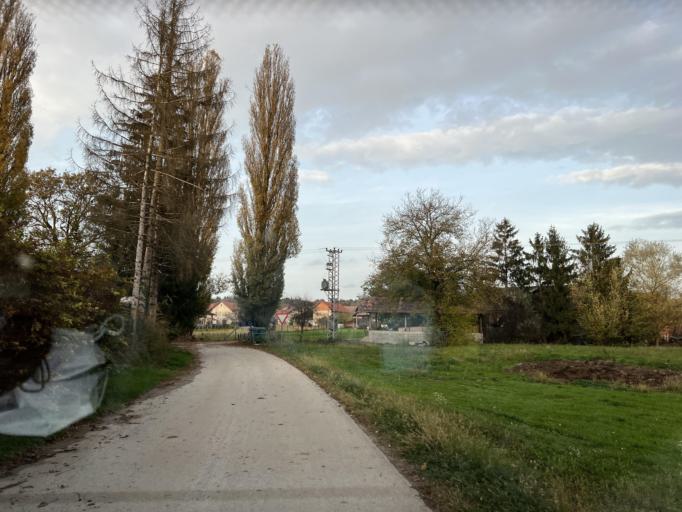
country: SI
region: Krsko
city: Leskovec pri Krskem
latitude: 45.8752
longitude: 15.4774
